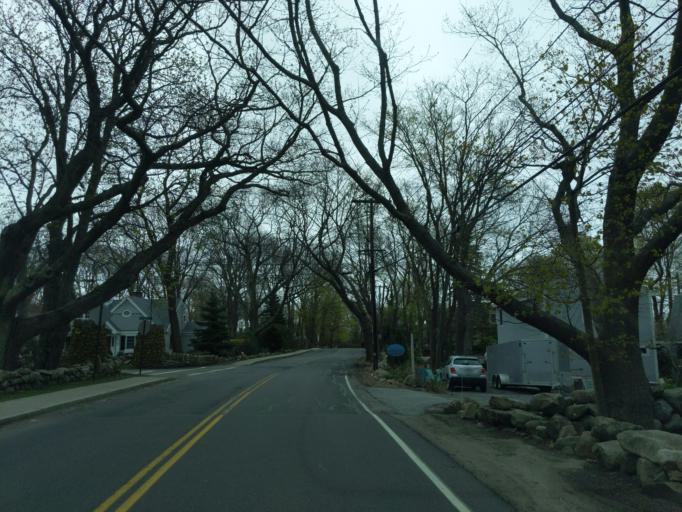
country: US
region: Massachusetts
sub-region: Essex County
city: Rockport
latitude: 42.6538
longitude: -70.6030
